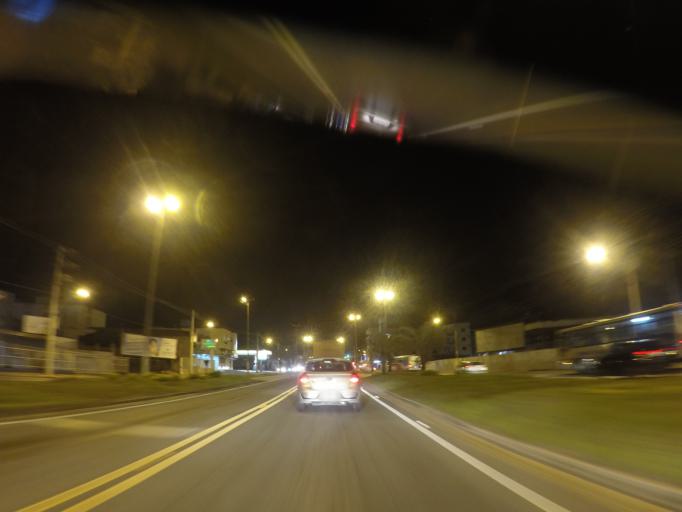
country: BR
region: Espirito Santo
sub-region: Linhares
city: Linhares
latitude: -19.3971
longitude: -40.0639
